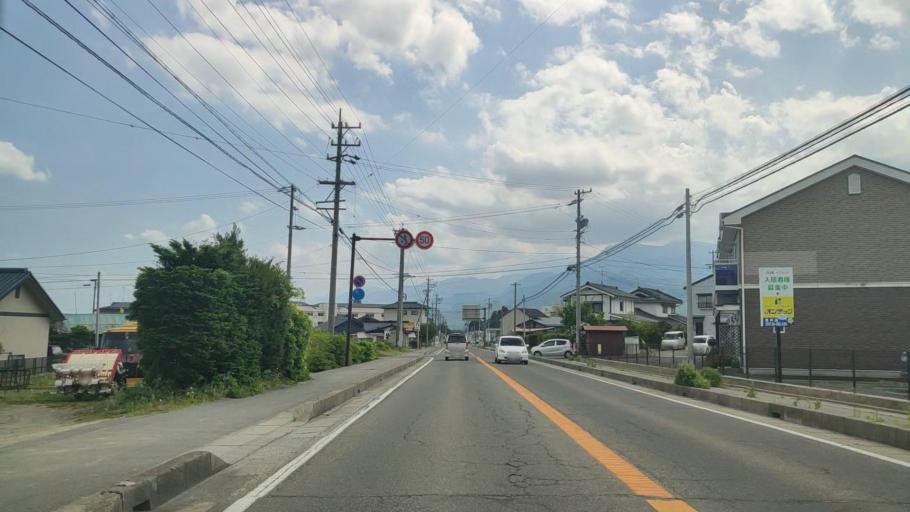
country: JP
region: Nagano
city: Omachi
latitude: 36.4804
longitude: 137.8508
